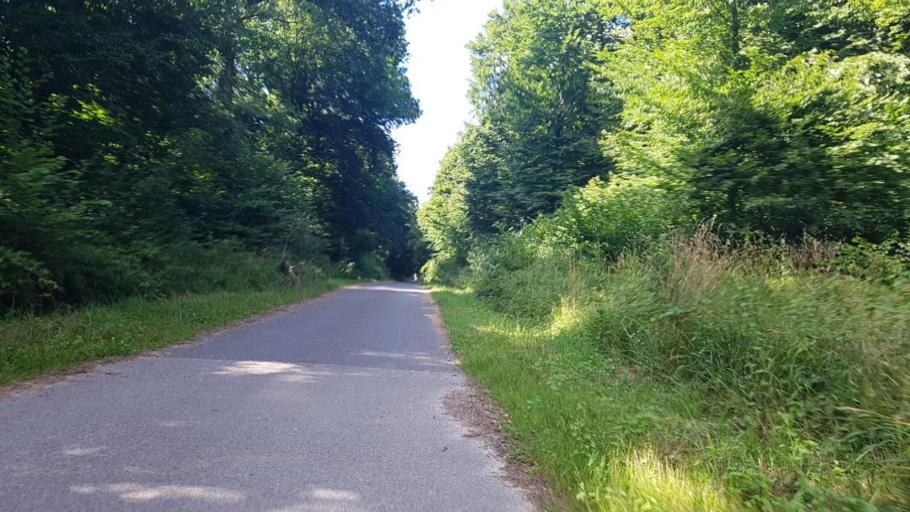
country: FR
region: Picardie
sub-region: Departement de l'Oise
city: Ver-sur-Launette
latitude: 49.1142
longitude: 2.6557
